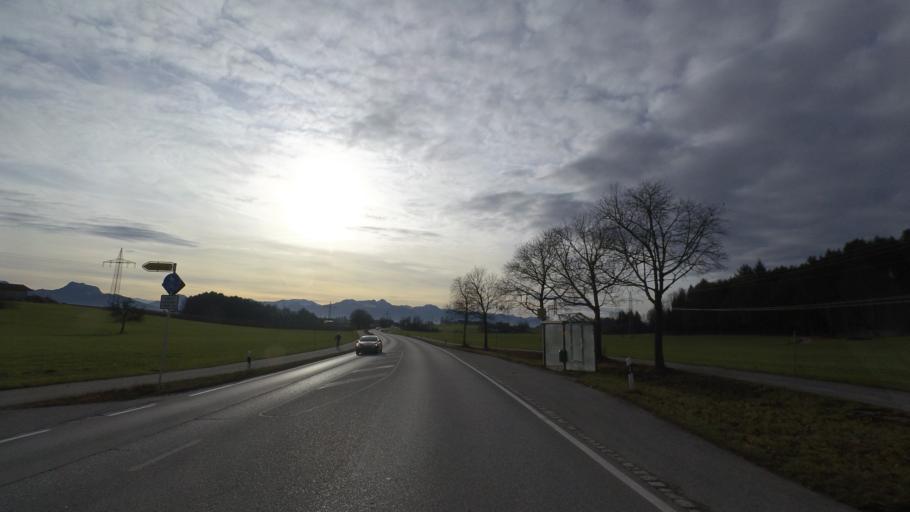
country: DE
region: Bavaria
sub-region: Upper Bavaria
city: Prutting
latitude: 47.8819
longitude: 12.1824
